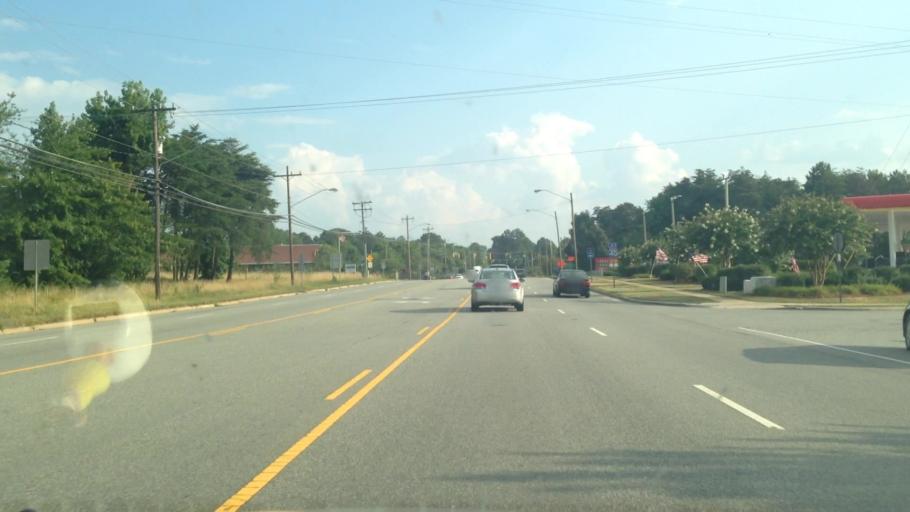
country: US
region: North Carolina
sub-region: Forsyth County
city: Kernersville
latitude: 36.0889
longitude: -80.0628
